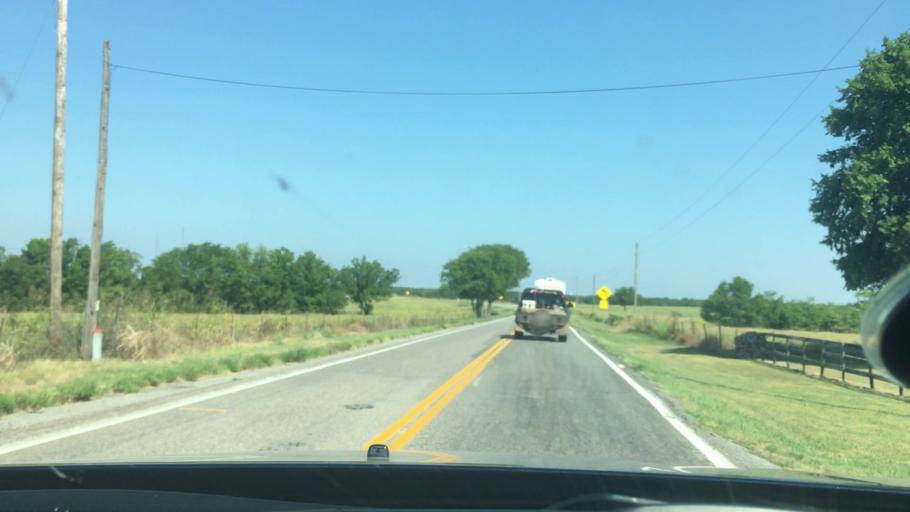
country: US
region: Oklahoma
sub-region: Johnston County
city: Tishomingo
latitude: 34.1849
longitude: -96.5153
